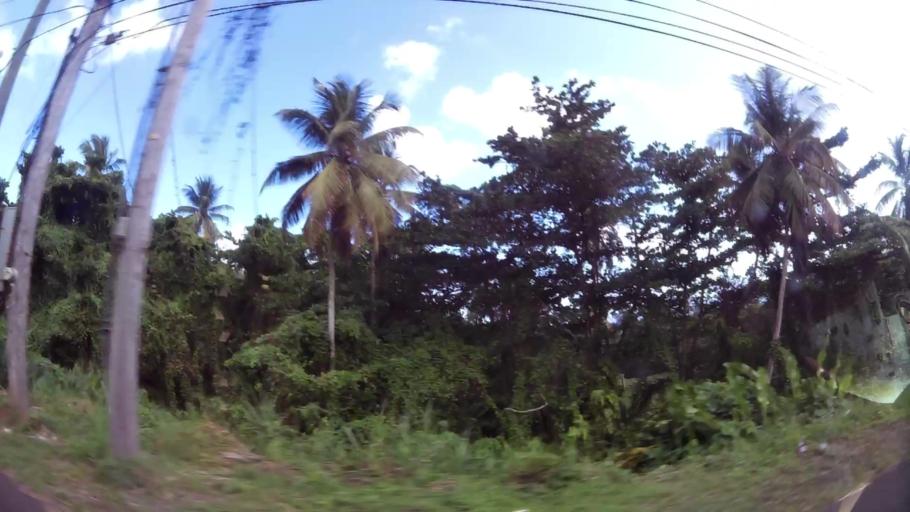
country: DM
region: Saint Andrew
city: Marigot
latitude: 15.5277
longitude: -61.2747
